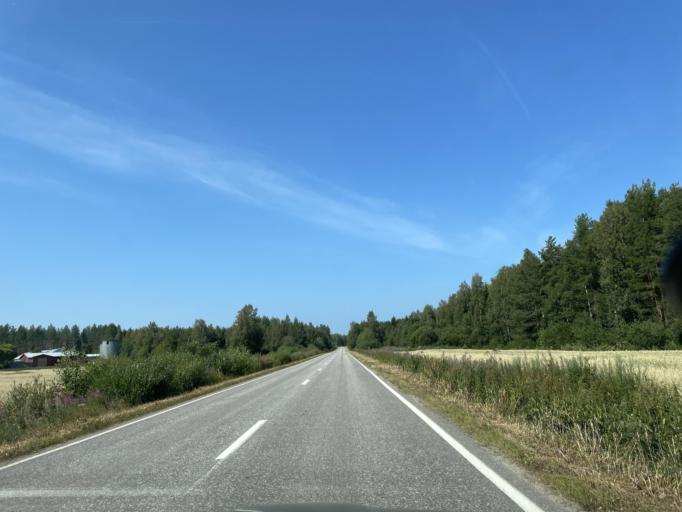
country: FI
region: Central Finland
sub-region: Saarijaervi-Viitasaari
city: Pihtipudas
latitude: 63.3649
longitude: 25.6442
